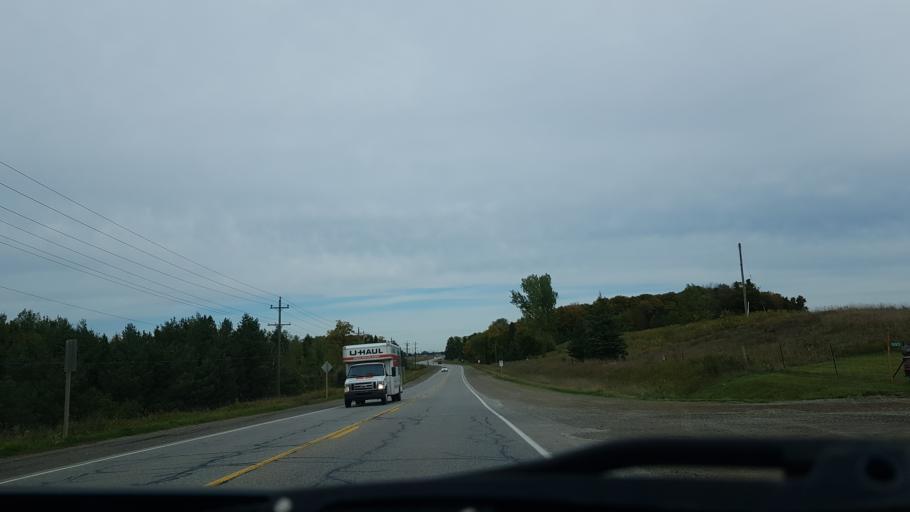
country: CA
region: Ontario
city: Orangeville
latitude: 43.8127
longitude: -80.0478
